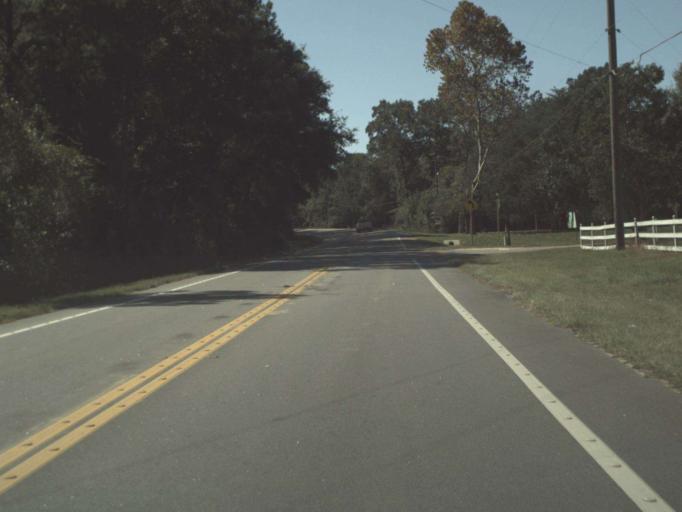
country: US
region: Alabama
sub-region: Covington County
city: Florala
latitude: 30.9910
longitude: -86.3375
